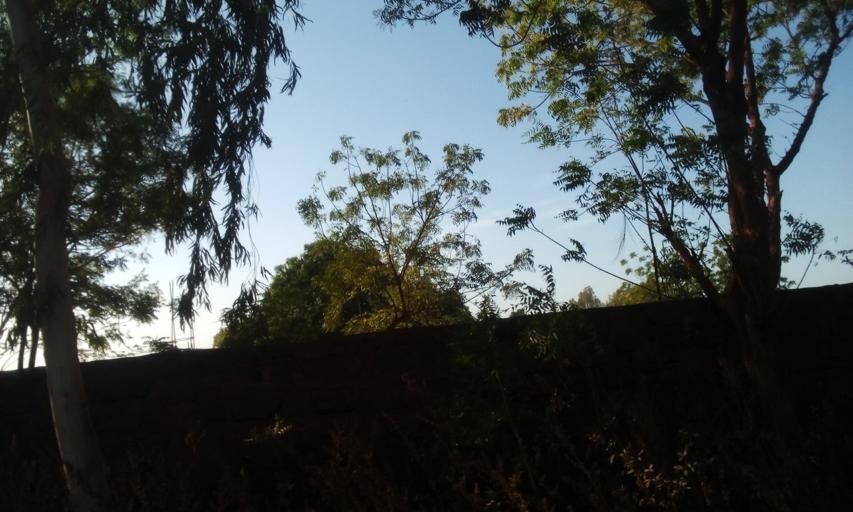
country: ML
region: Bamako
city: Bamako
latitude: 12.6438
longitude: -7.9051
